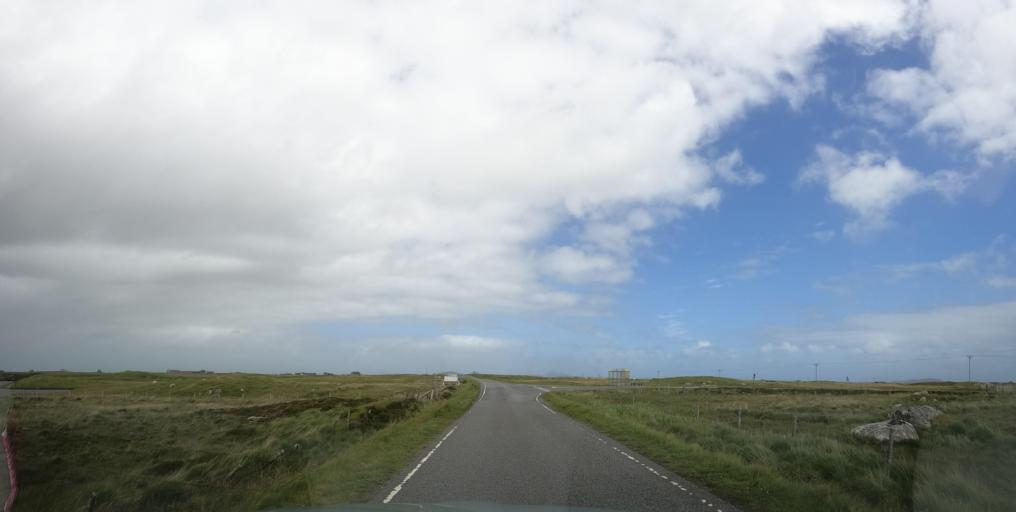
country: GB
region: Scotland
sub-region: Eilean Siar
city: Benbecula
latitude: 57.3826
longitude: -7.3407
